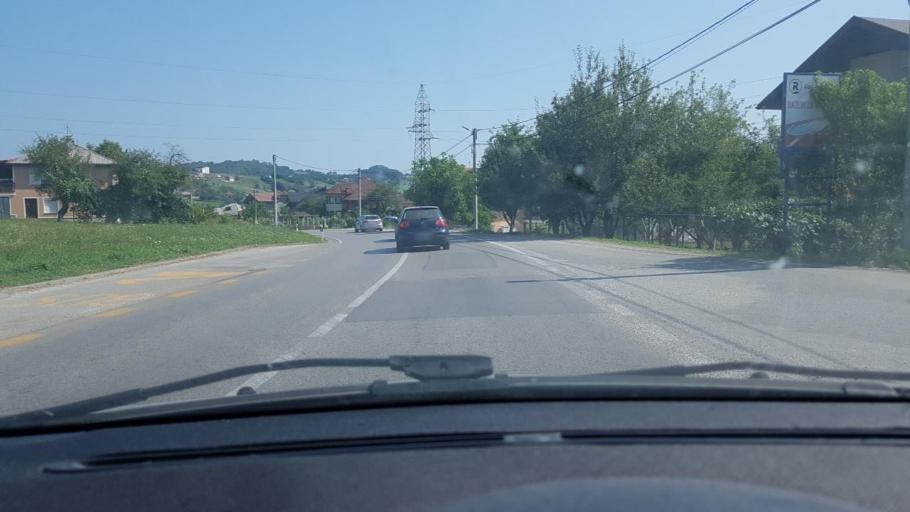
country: BA
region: Federation of Bosnia and Herzegovina
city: Velika Kladusa
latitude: 45.1758
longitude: 15.8209
